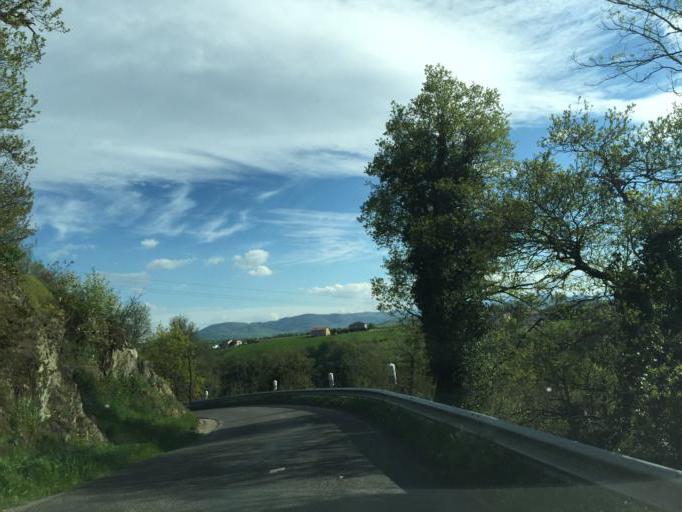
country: FR
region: Rhone-Alpes
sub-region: Departement du Rhone
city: Saint-Andeol-le-Chateau
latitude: 45.5797
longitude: 4.6993
